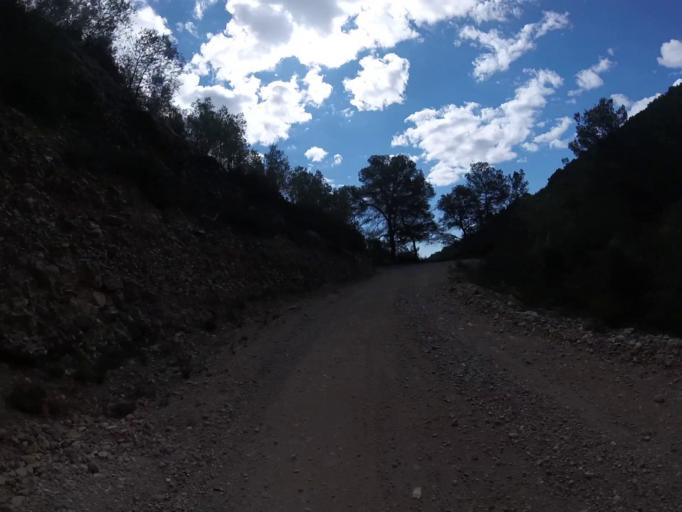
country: ES
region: Valencia
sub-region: Provincia de Castello
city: Santa Magdalena de Pulpis
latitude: 40.3119
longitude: 0.3261
